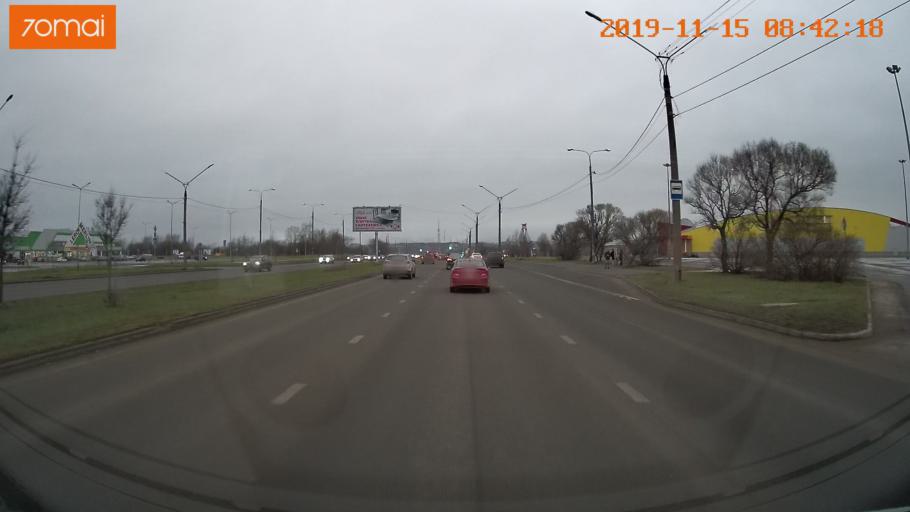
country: RU
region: Vologda
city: Cherepovets
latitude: 59.1020
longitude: 37.9087
